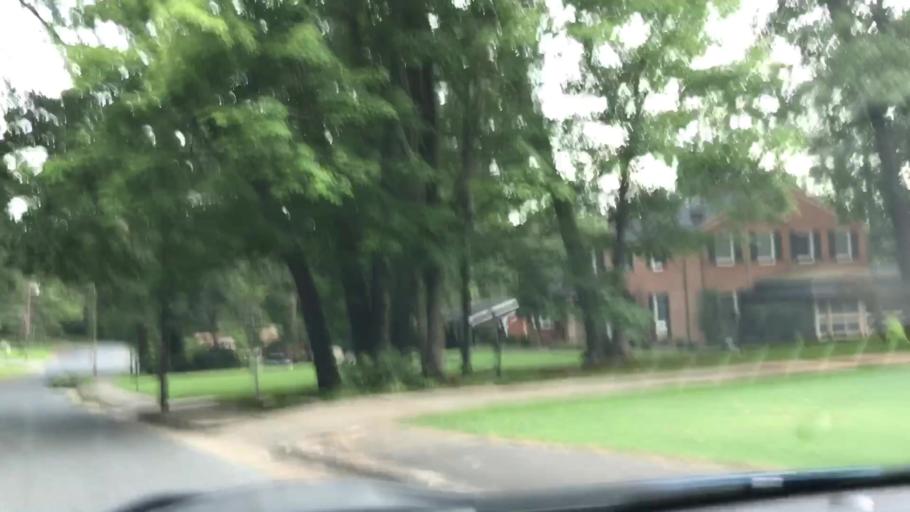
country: US
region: North Carolina
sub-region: Randolph County
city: Asheboro
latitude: 35.7009
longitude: -79.8056
